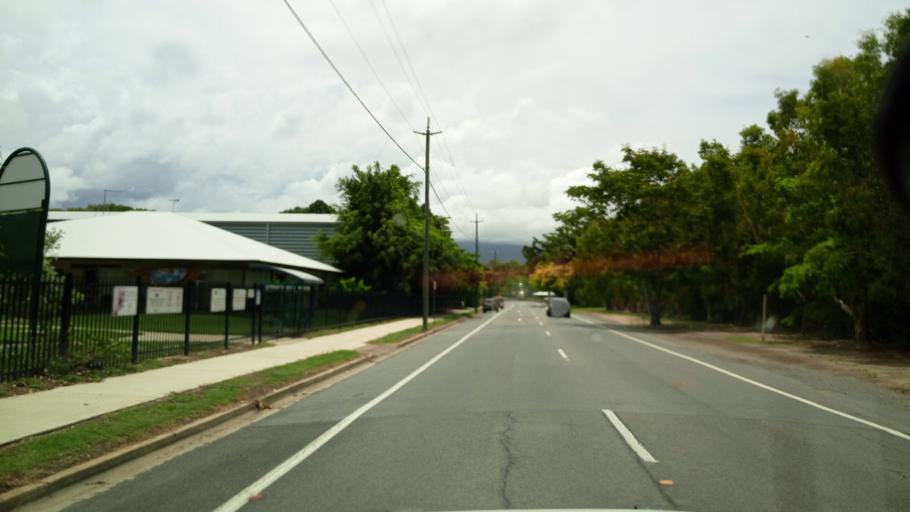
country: AU
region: Queensland
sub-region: Cairns
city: Redlynch
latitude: -16.8525
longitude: 145.7451
